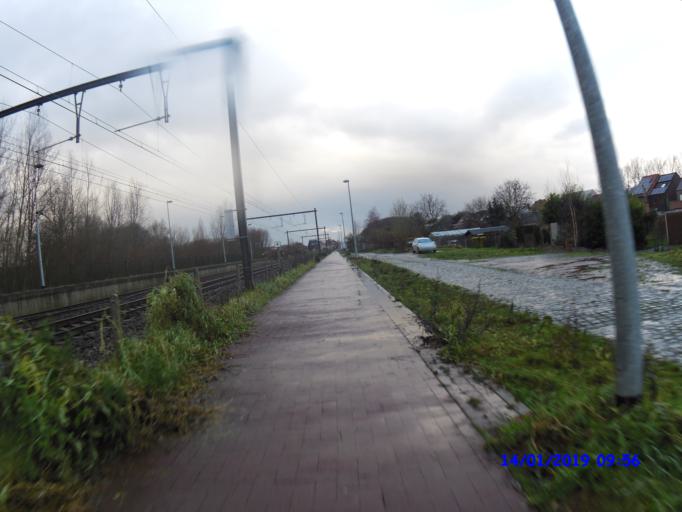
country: BE
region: Flanders
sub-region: Provincie Oost-Vlaanderen
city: Lebbeke
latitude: 50.9907
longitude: 4.1544
